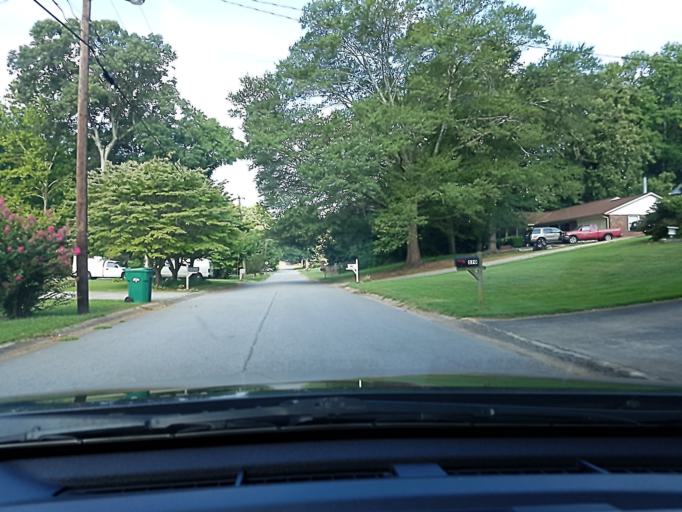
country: US
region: Georgia
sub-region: Cobb County
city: Mableton
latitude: 33.8420
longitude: -84.5709
